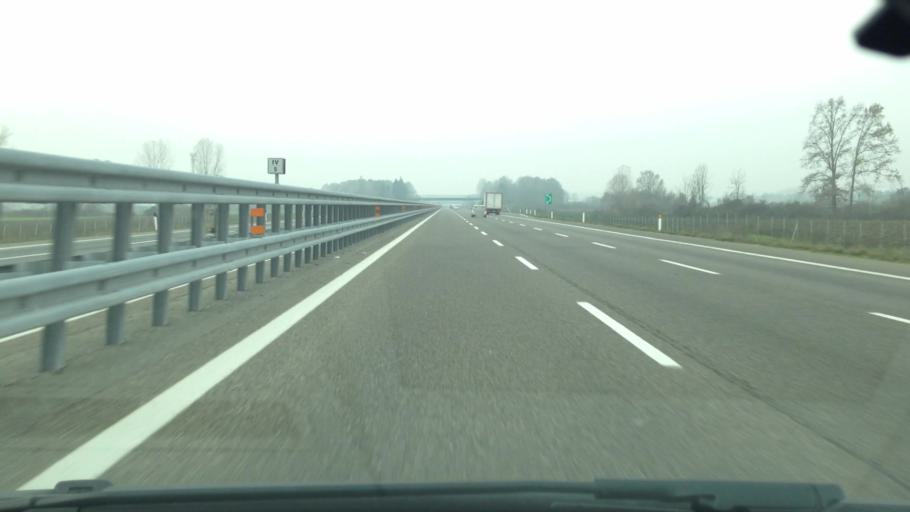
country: IT
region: Piedmont
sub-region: Provincia di Torino
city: Pessione
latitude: 44.9547
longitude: 7.8556
